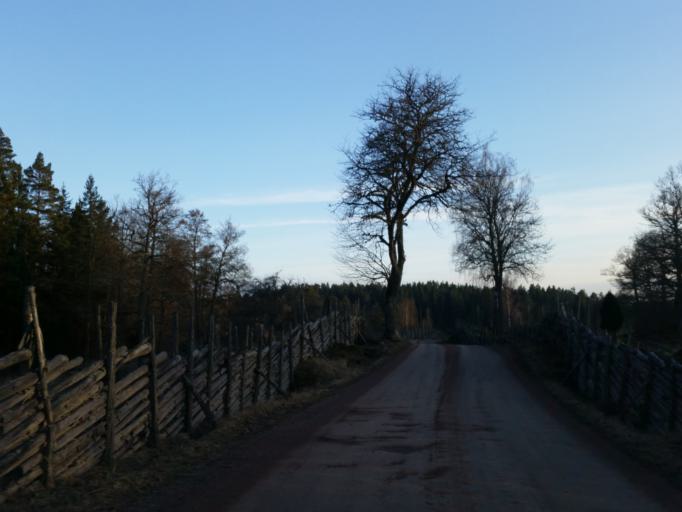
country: SE
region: Kalmar
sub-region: Oskarshamns Kommun
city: Oskarshamn
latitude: 57.3412
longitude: 16.4699
